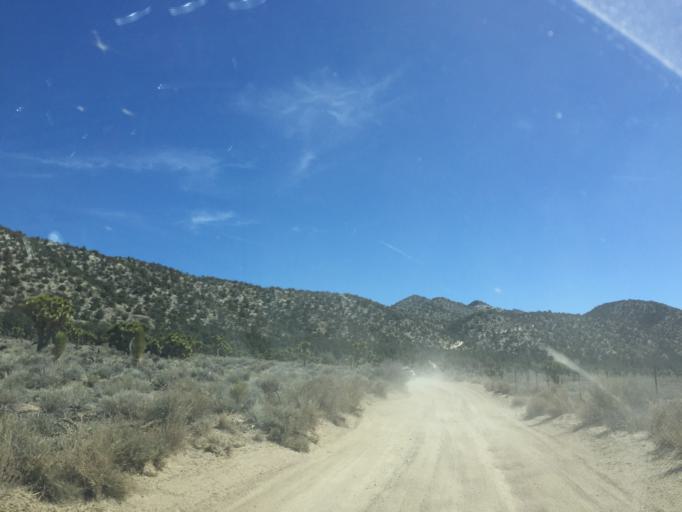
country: US
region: California
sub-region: San Bernardino County
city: Big Bear City
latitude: 34.2556
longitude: -116.7145
